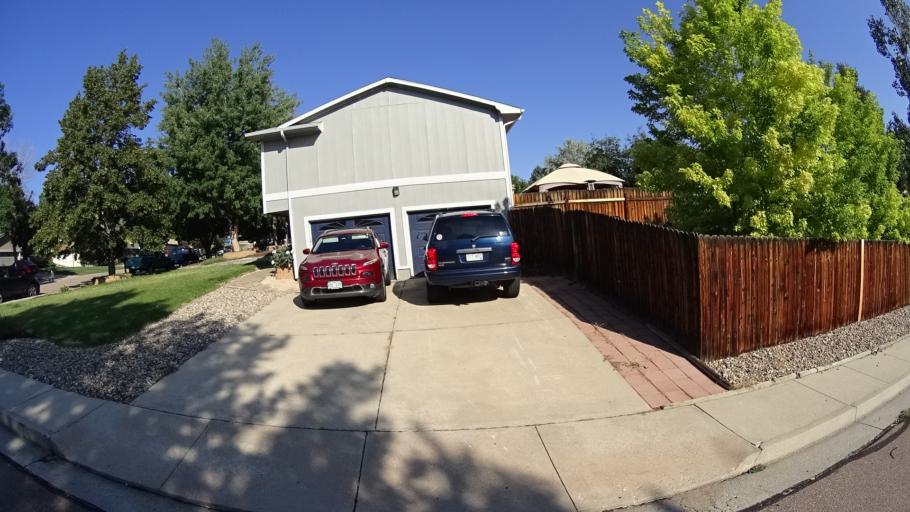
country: US
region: Colorado
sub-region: El Paso County
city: Colorado Springs
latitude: 38.8845
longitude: -104.8396
